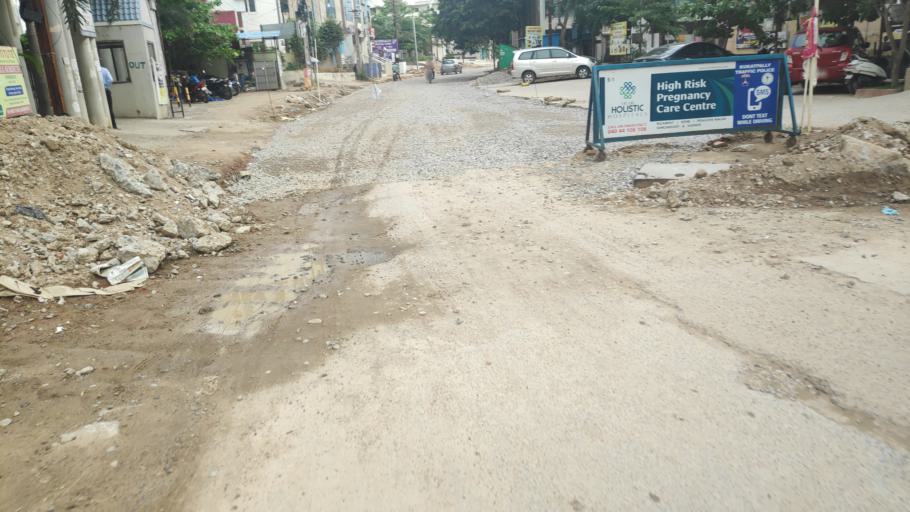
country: IN
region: Telangana
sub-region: Rangareddi
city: Kukatpalli
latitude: 17.5142
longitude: 78.3883
